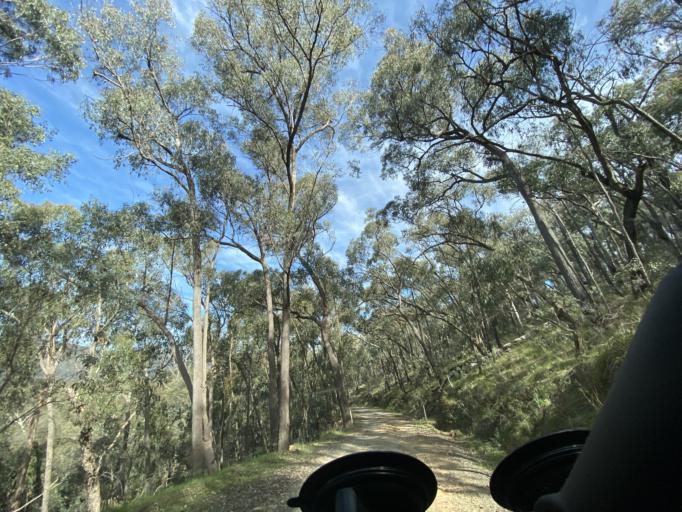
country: AU
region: Victoria
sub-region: Mansfield
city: Mansfield
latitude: -36.7991
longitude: 146.1153
